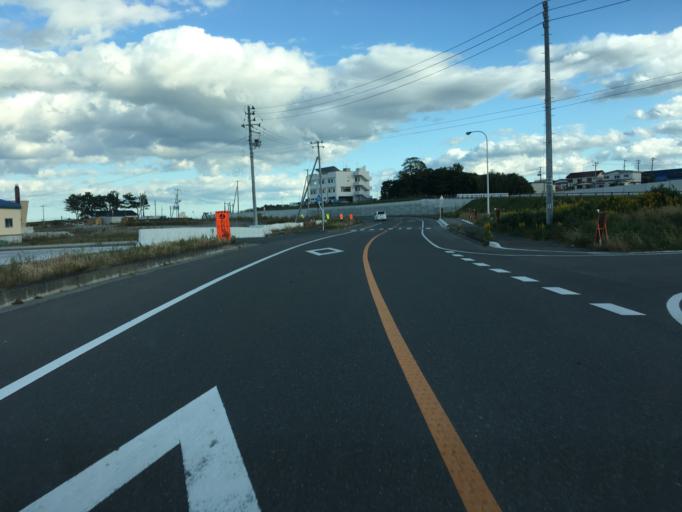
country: JP
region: Miyagi
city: Marumori
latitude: 37.8305
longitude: 140.9605
